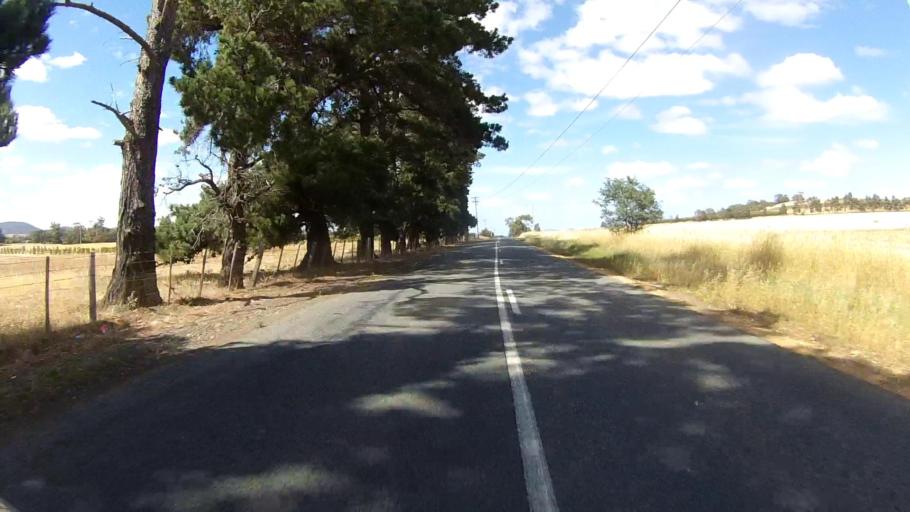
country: AU
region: Tasmania
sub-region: Sorell
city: Sorell
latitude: -42.6395
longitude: 147.4332
